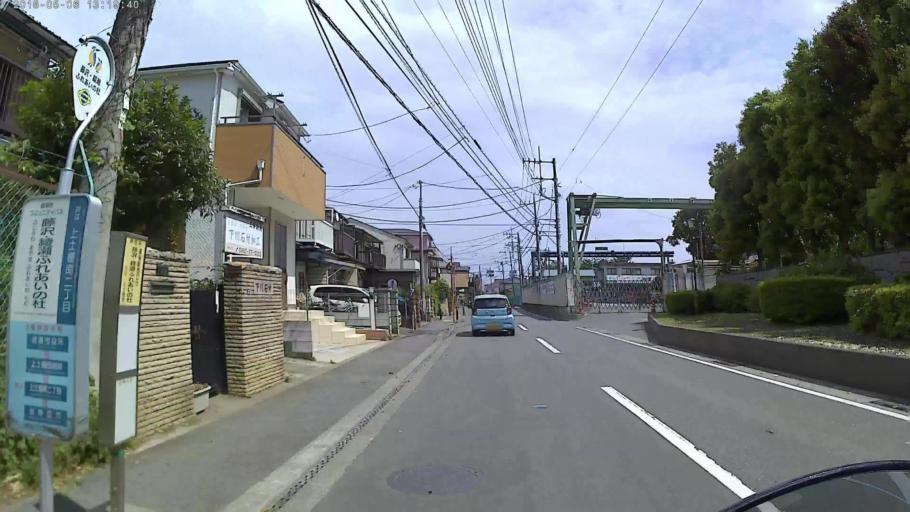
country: JP
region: Kanagawa
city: Minami-rinkan
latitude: 35.4135
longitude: 139.4419
